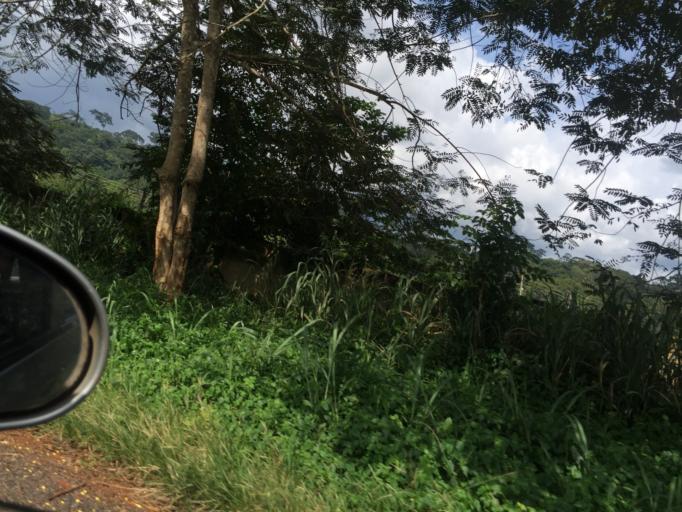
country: GH
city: Mpraeso
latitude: 6.6034
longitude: -0.7395
